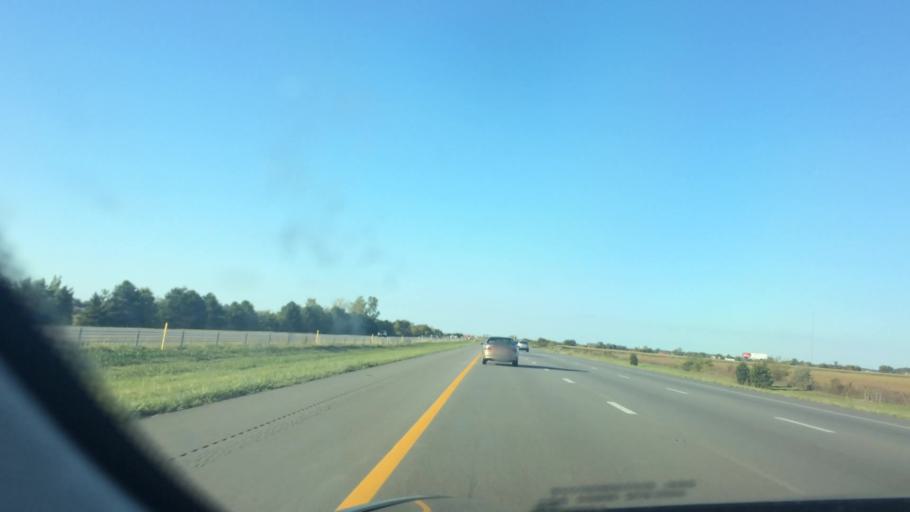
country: US
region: Ohio
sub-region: Wood County
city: Bowling Green
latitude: 41.4125
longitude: -83.6157
